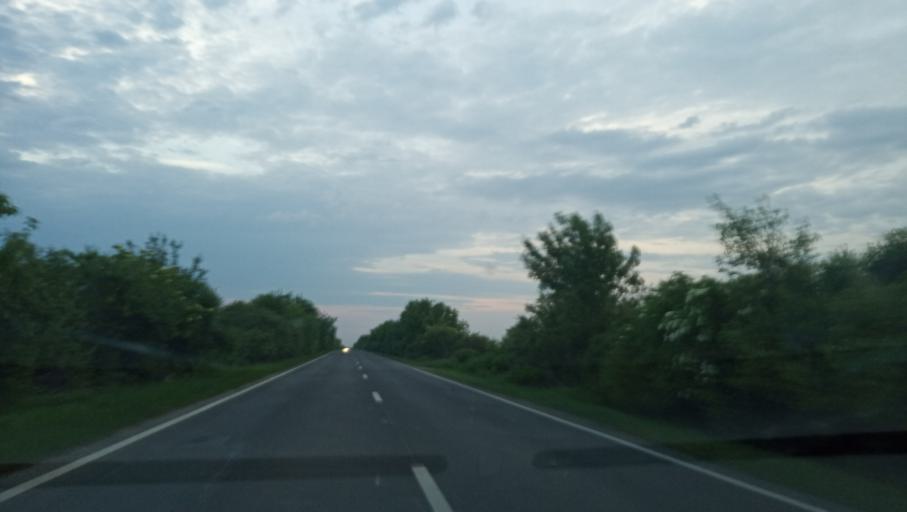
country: RO
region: Timis
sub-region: Comuna Jebel
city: Jebel
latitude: 45.5164
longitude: 21.2348
